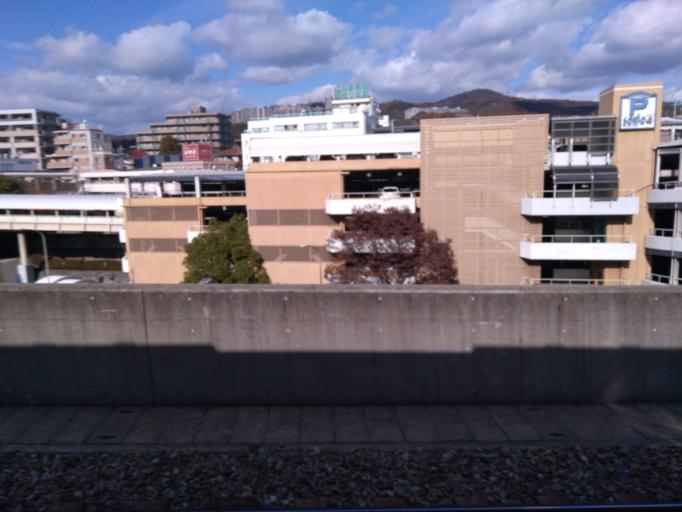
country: JP
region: Hyogo
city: Takarazuka
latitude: 34.8100
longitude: 135.3434
